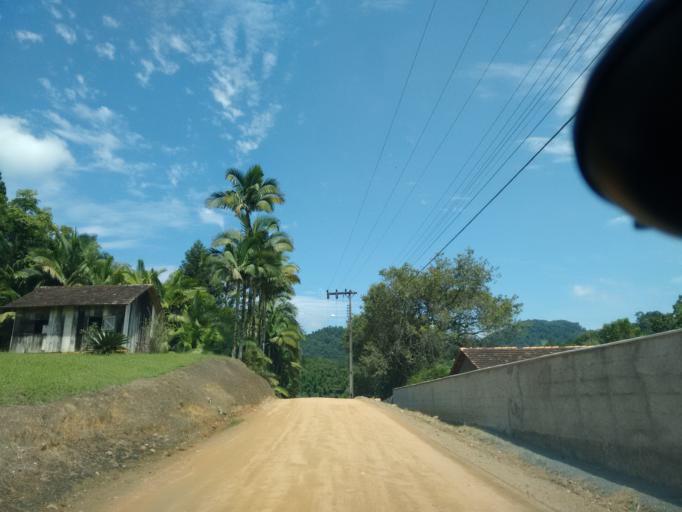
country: BR
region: Santa Catarina
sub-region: Indaial
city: Indaial
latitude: -26.8467
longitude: -49.1579
